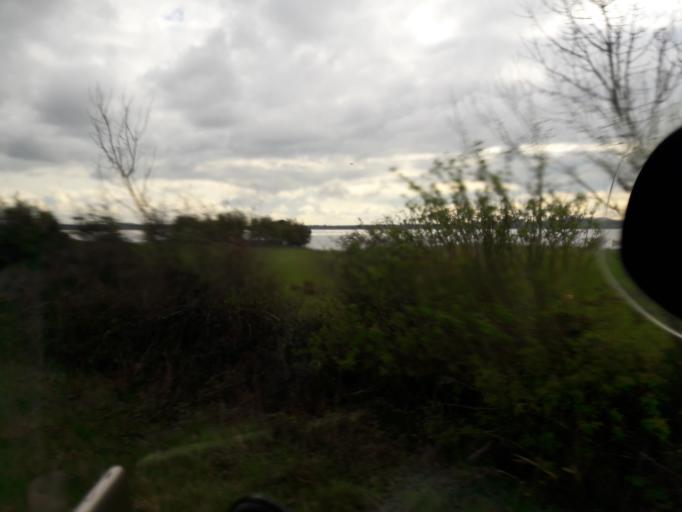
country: IE
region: Leinster
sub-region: An Iarmhi
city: An Muileann gCearr
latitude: 53.5859
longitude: -7.3822
